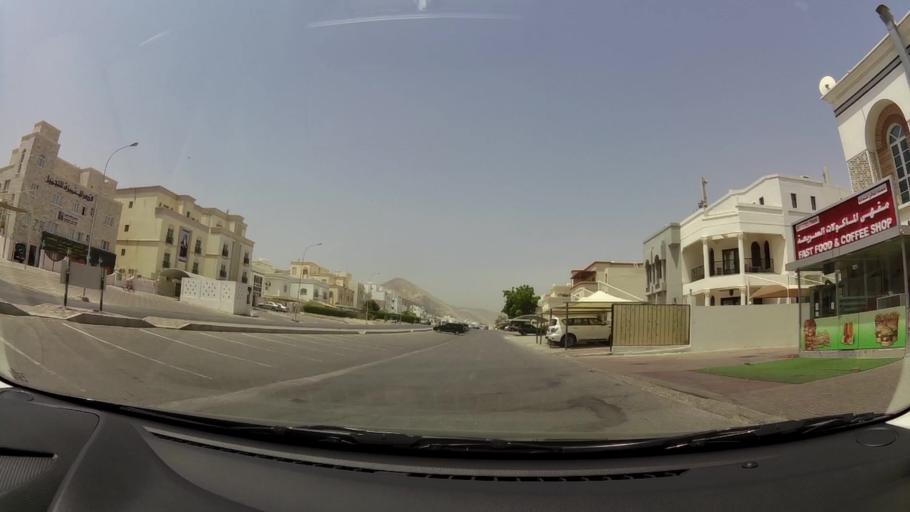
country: OM
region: Muhafazat Masqat
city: Bawshar
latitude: 23.5868
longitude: 58.4397
